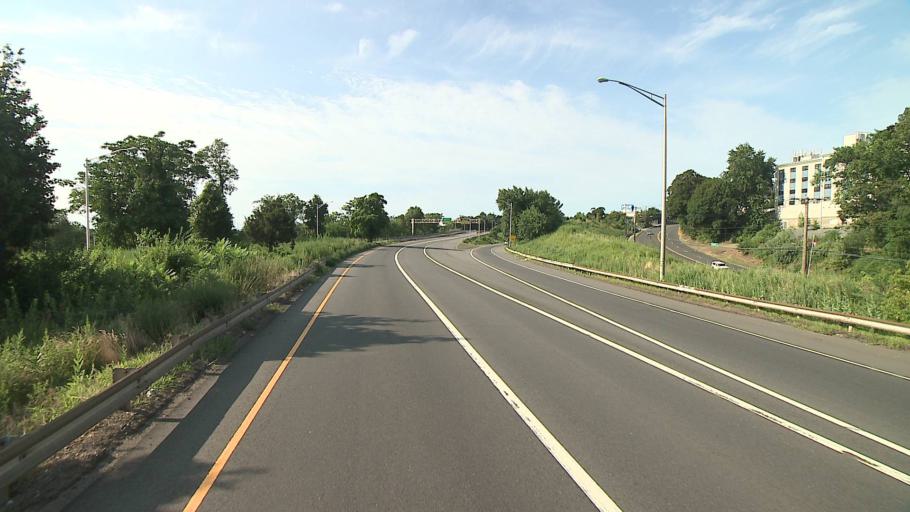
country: US
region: Connecticut
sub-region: Fairfield County
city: Norwalk
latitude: 41.1097
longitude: -73.4192
